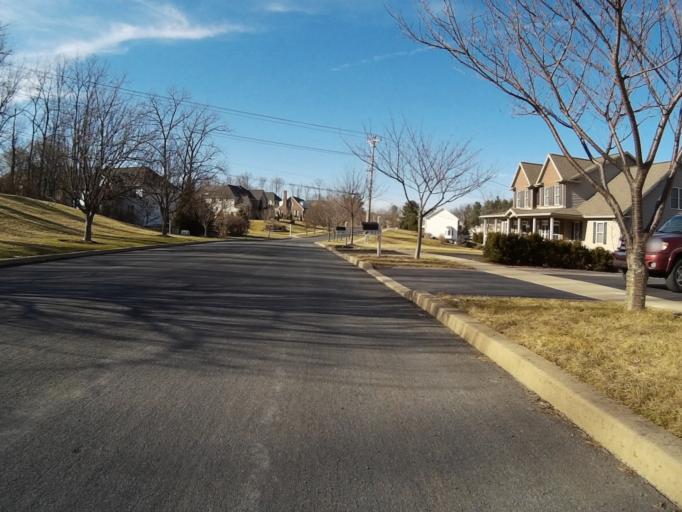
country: US
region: Pennsylvania
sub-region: Centre County
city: State College
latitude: 40.7945
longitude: -77.8842
